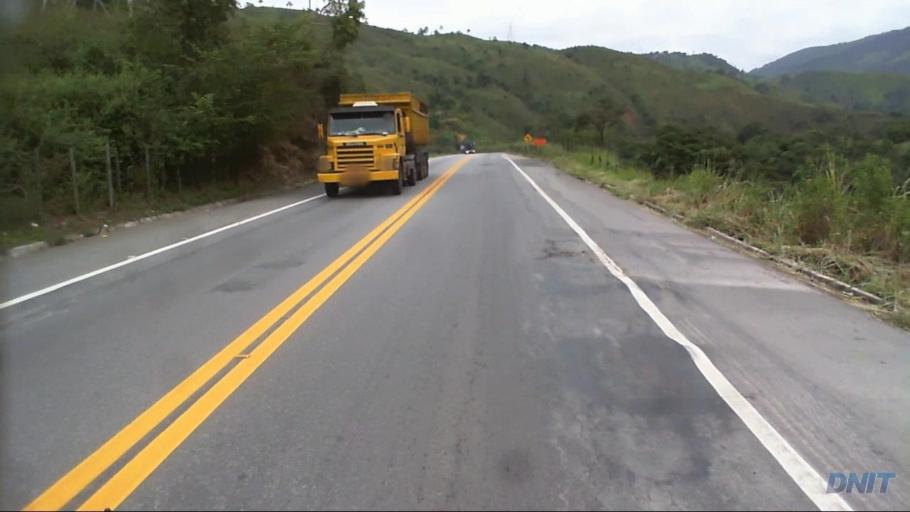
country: BR
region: Minas Gerais
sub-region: Timoteo
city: Timoteo
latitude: -19.6166
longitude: -42.7742
